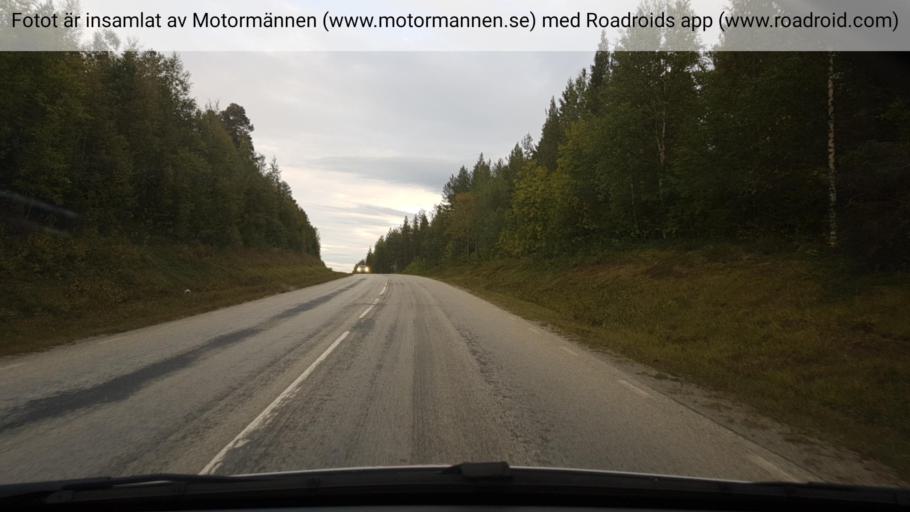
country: SE
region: Jaemtland
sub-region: Harjedalens Kommun
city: Sveg
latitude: 62.4209
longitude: 13.5386
